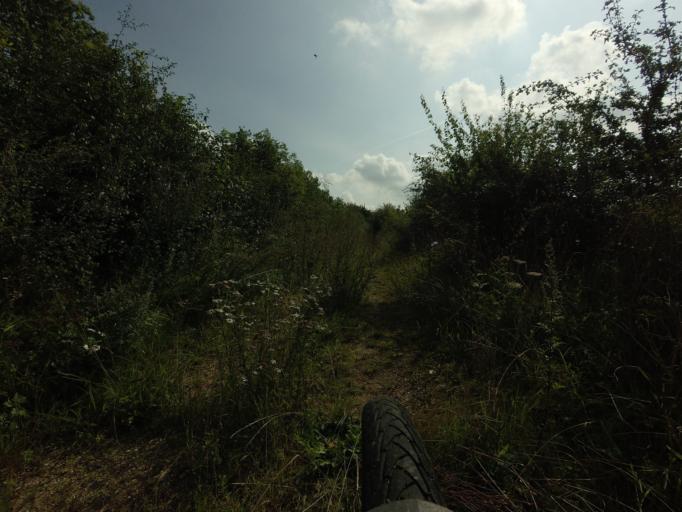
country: DK
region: Zealand
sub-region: Naestved Kommune
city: Naestved
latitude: 55.2173
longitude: 11.8238
